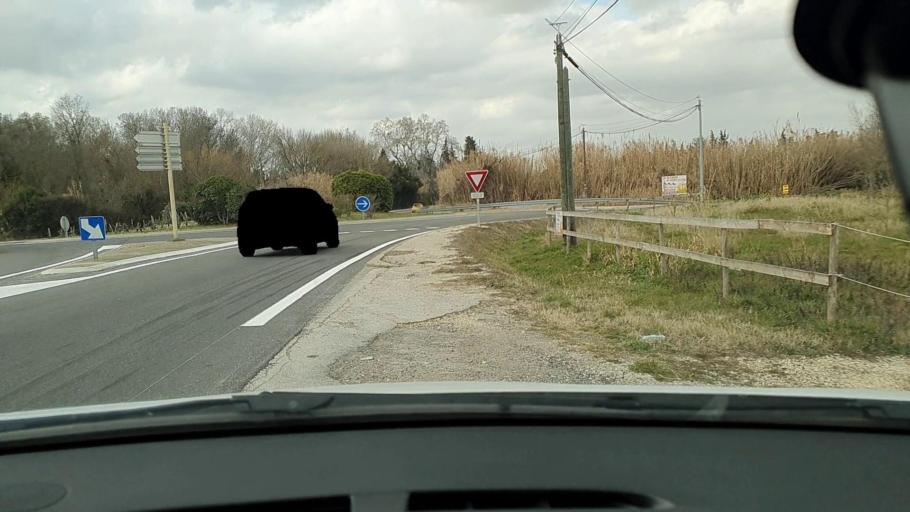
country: FR
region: Languedoc-Roussillon
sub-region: Departement du Gard
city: Meynes
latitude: 43.8798
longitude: 4.5759
